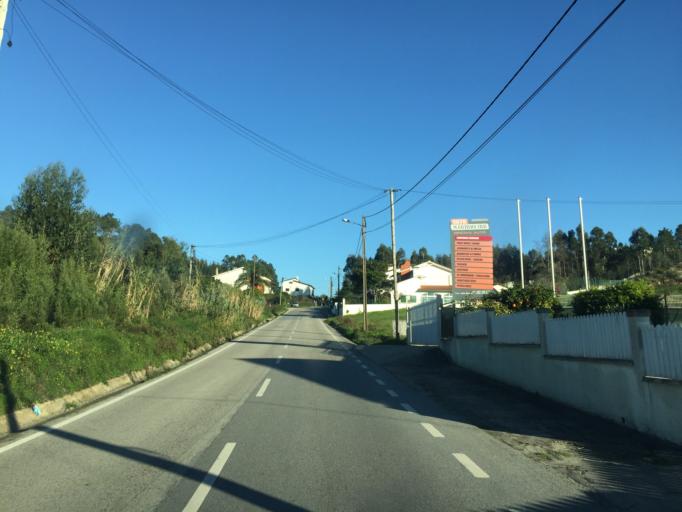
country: PT
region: Coimbra
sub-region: Figueira da Foz
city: Tavarede
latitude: 40.1656
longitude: -8.8268
